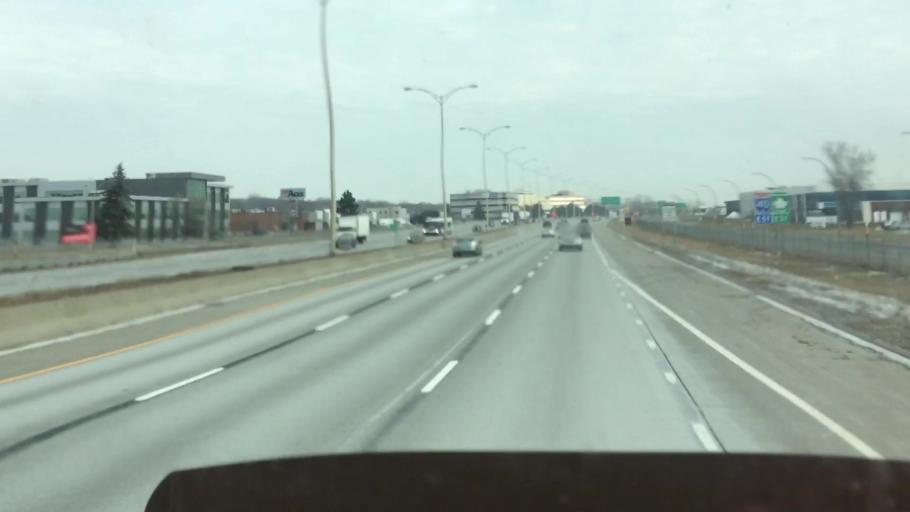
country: CA
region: Quebec
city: Dollard-Des Ormeaux
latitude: 45.4859
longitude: -73.7808
